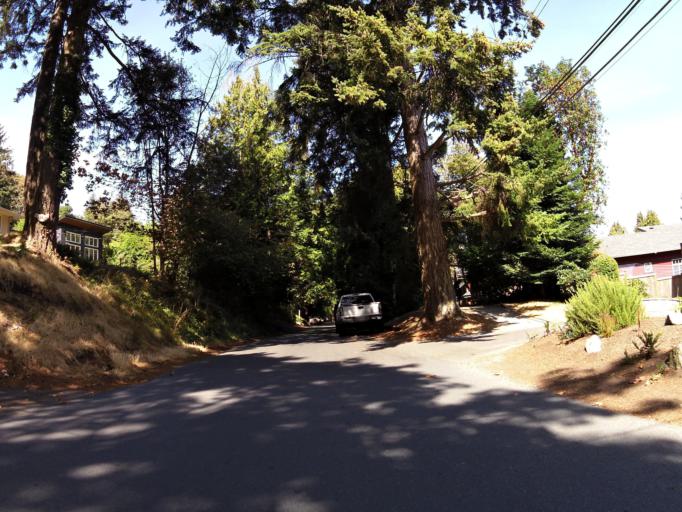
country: CA
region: British Columbia
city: Victoria
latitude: 48.5235
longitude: -123.3724
